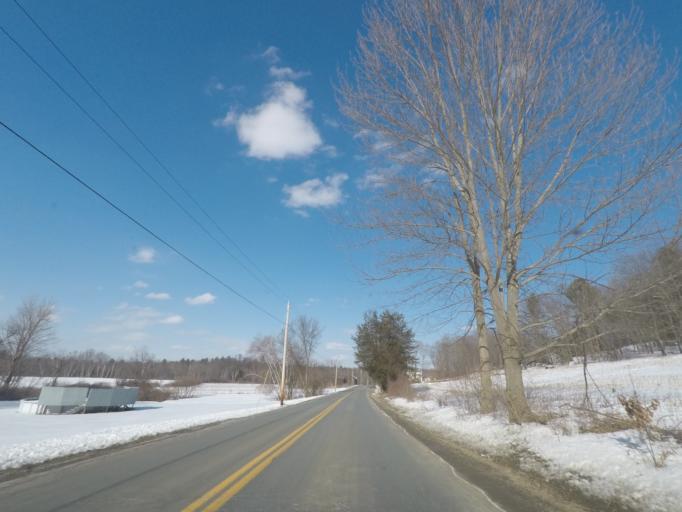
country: US
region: New York
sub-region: Saratoga County
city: Stillwater
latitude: 42.8787
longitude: -73.5789
